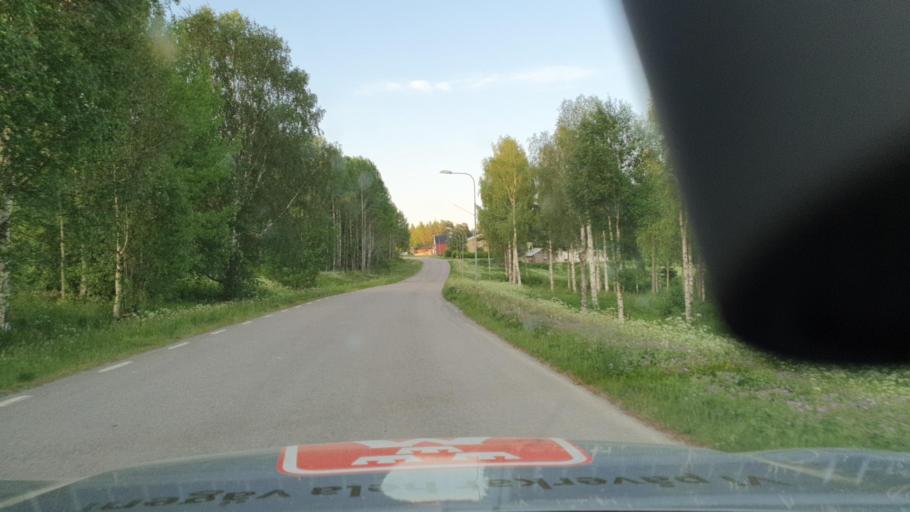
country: SE
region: Norrbotten
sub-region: Bodens Kommun
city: Boden
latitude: 66.0492
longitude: 21.7728
